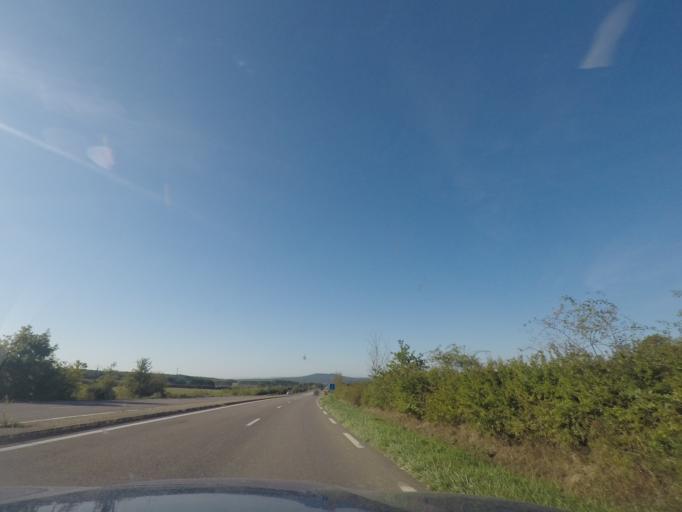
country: FR
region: Lorraine
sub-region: Departement de la Moselle
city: Hettange-Grande
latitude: 49.4292
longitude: 6.1661
